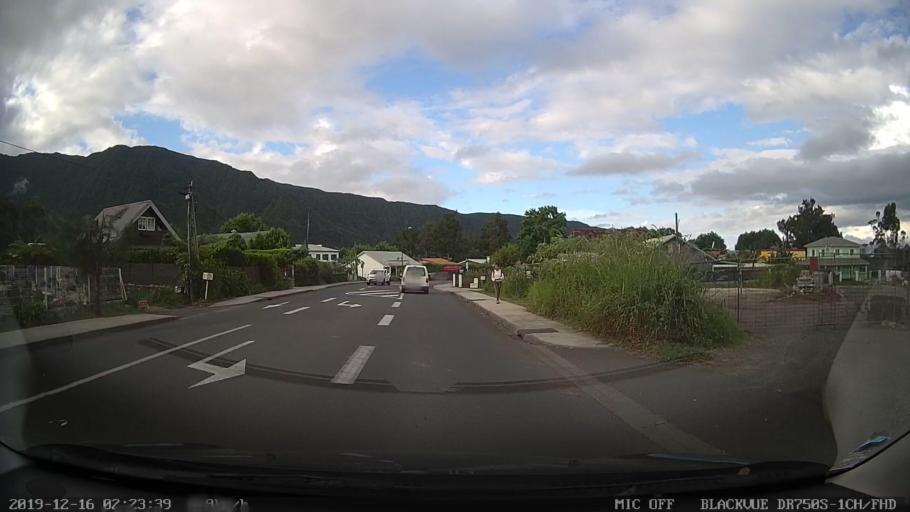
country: RE
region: Reunion
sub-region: Reunion
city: Salazie
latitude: -21.1420
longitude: 55.6217
